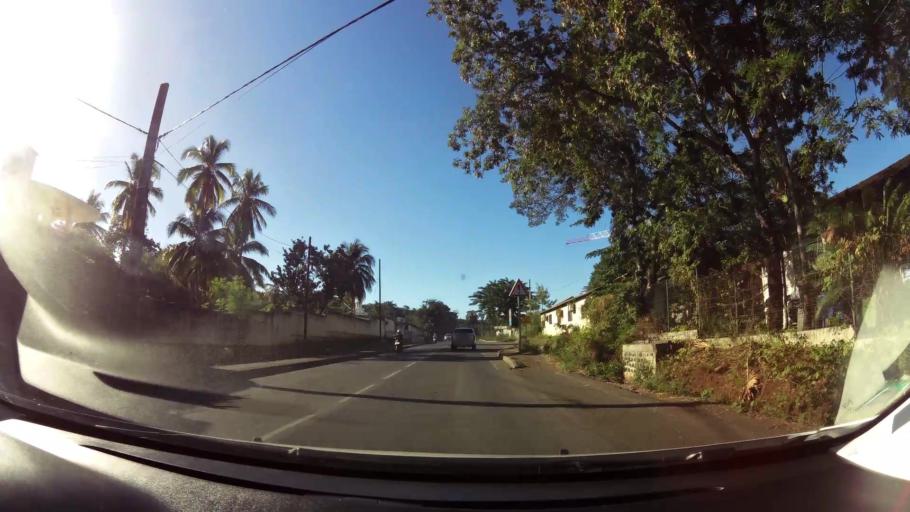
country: YT
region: Mamoudzou
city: Mamoudzou
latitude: -12.7657
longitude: 45.2252
